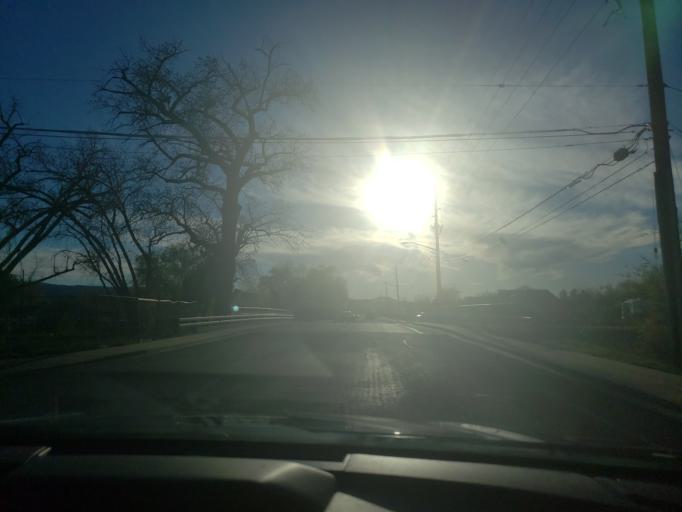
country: US
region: Colorado
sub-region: Mesa County
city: Fruita
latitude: 39.1643
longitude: -108.7383
